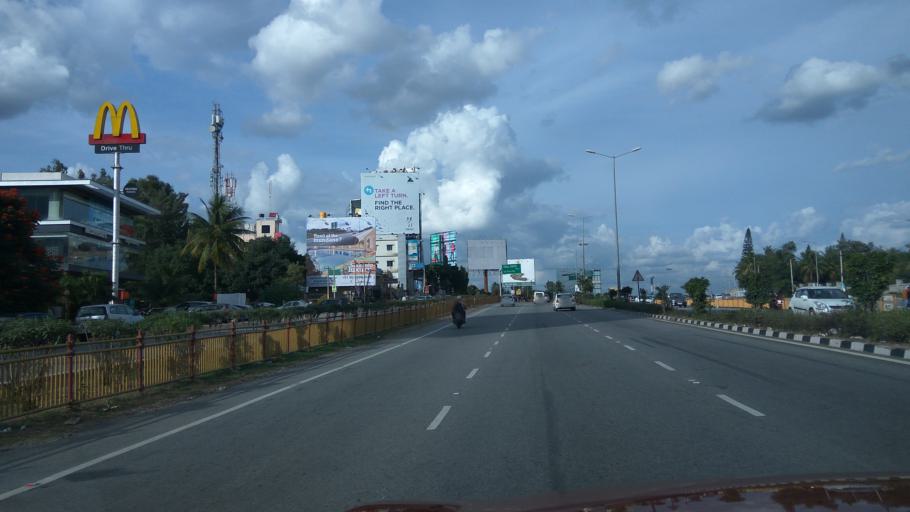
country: IN
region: Karnataka
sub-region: Bangalore Rural
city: Devanhalli
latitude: 13.1895
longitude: 77.6451
